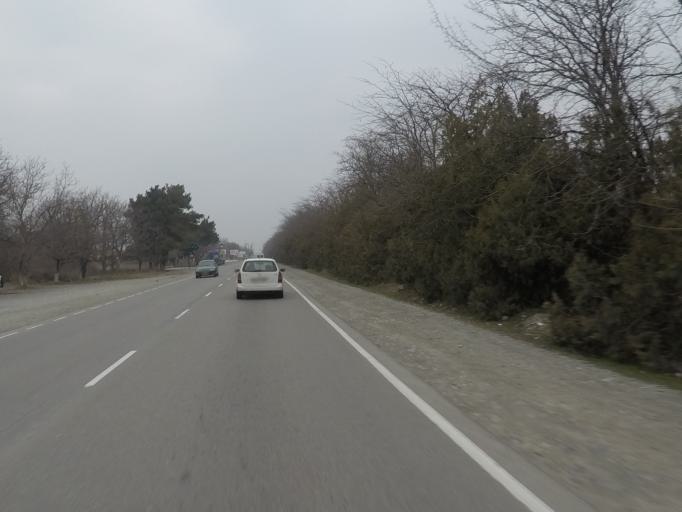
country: GE
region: Mtskheta-Mtianeti
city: Mtskheta
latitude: 41.8998
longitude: 44.7206
